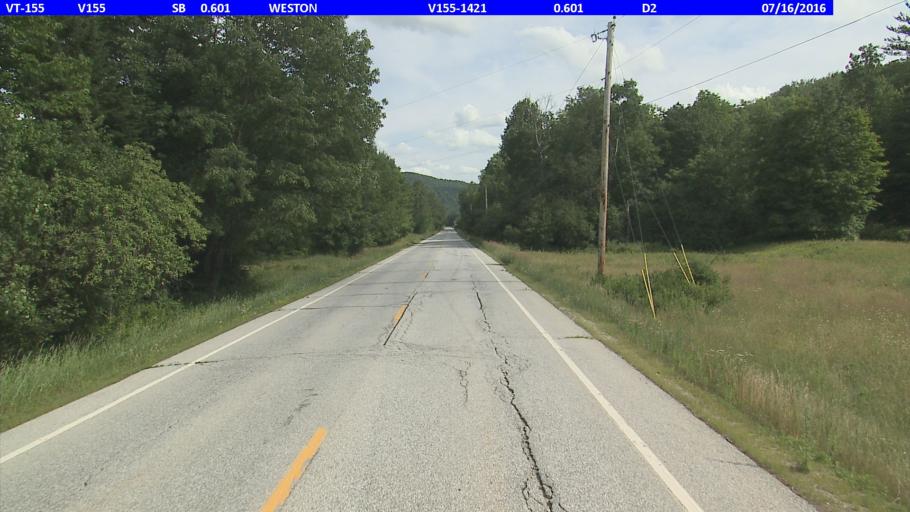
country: US
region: Vermont
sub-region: Windsor County
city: Chester
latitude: 43.3449
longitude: -72.7896
